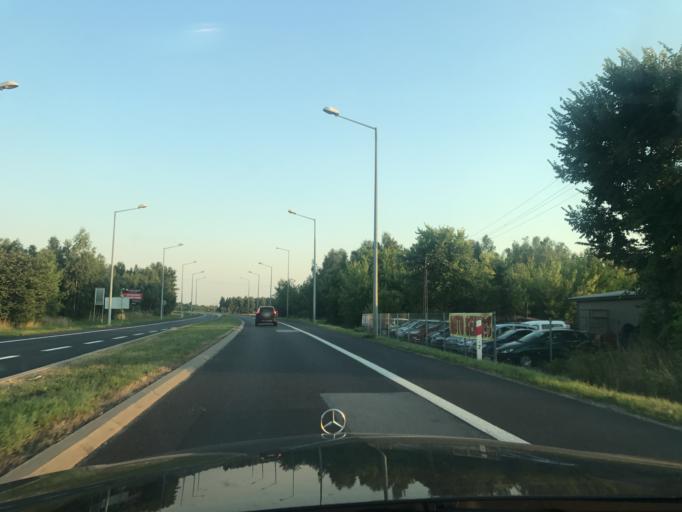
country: PL
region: Lublin Voivodeship
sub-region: Powiat lubartowski
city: Lubartow
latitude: 51.4618
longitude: 22.5760
